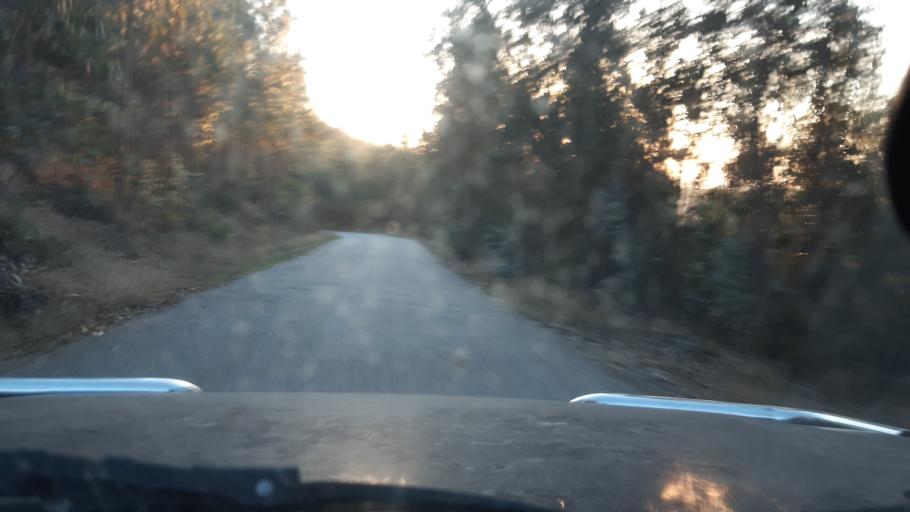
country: PT
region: Aveiro
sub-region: Agueda
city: Aguada de Cima
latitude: 40.5634
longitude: -8.3452
